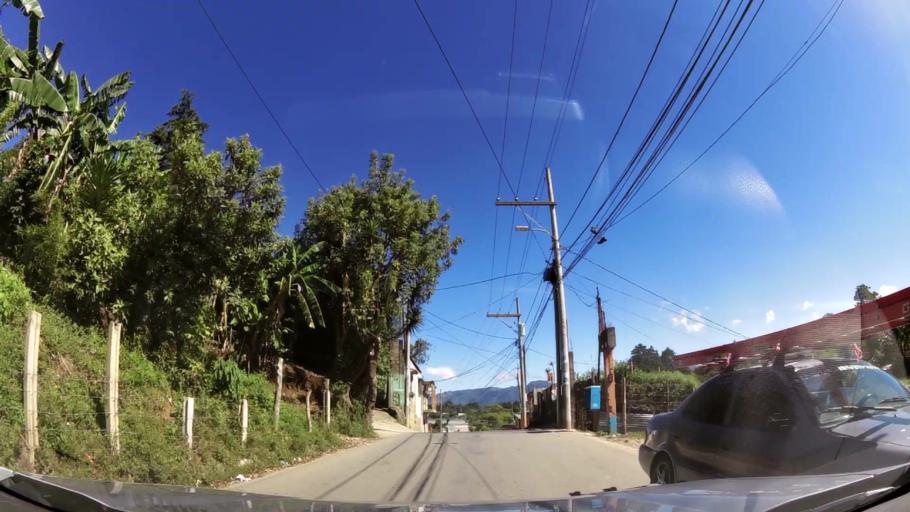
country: GT
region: Guatemala
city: San Jose Pinula
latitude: 14.5230
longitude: -90.4179
